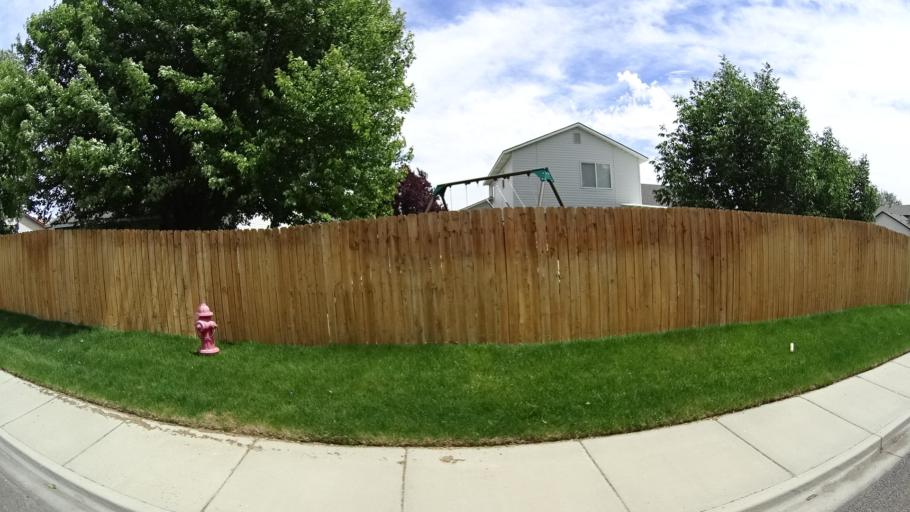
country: US
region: Idaho
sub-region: Ada County
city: Garden City
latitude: 43.6171
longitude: -116.3041
